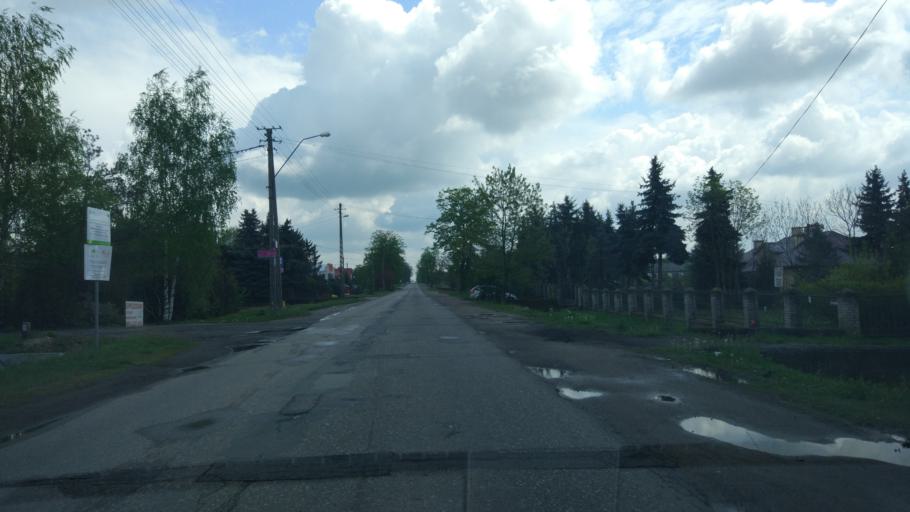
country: PL
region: Lodz Voivodeship
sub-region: Powiat kutnowski
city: Kutno
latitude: 52.2269
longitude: 19.3911
